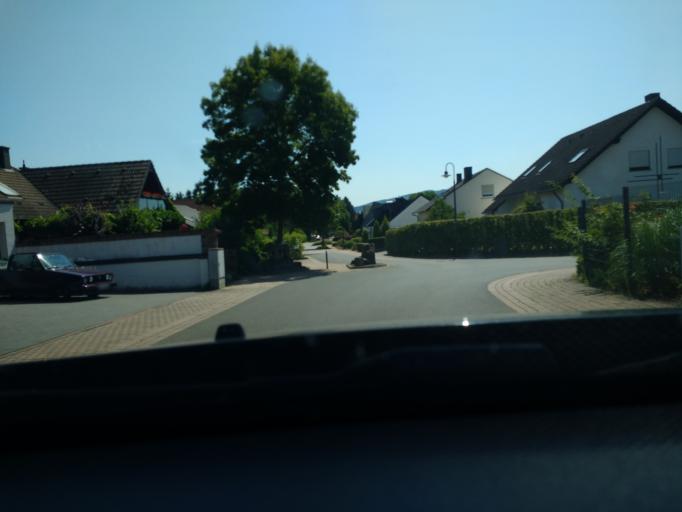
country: DE
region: Rheinland-Pfalz
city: Neuerburg
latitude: 49.9888
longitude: 6.9420
